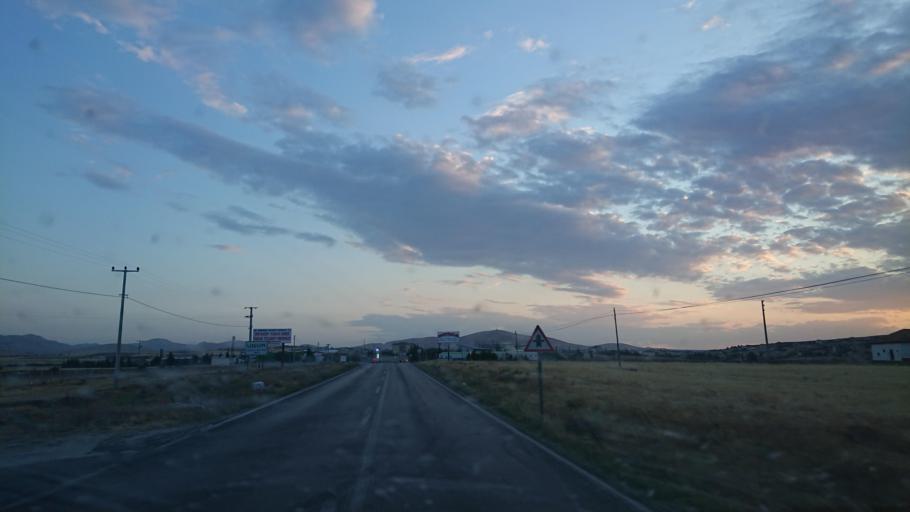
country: TR
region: Aksaray
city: Balci
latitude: 38.7597
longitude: 34.0830
